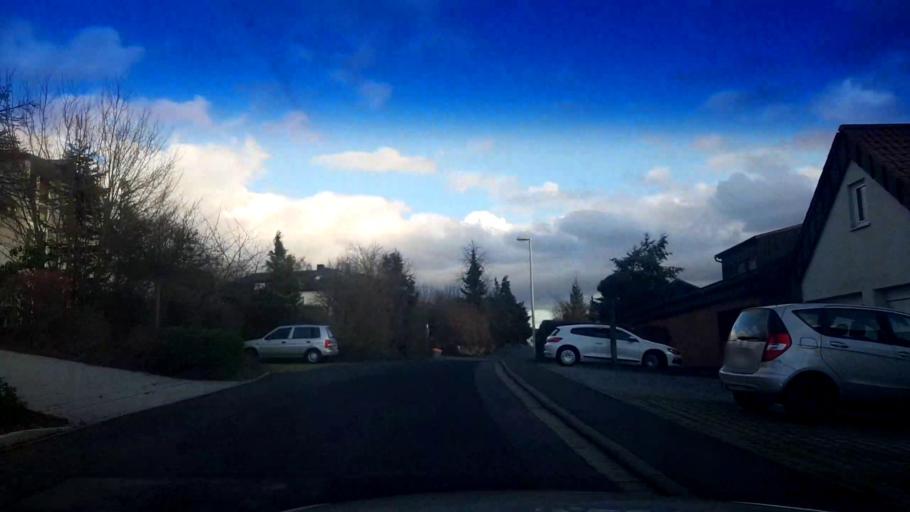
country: DE
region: Bavaria
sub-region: Upper Franconia
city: Buttenheim
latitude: 49.8089
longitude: 11.0336
